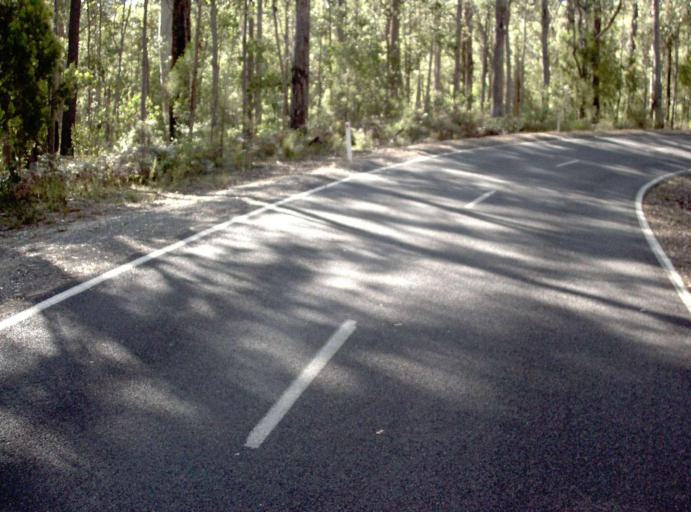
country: AU
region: Victoria
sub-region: East Gippsland
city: Lakes Entrance
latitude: -37.5852
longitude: 148.5357
